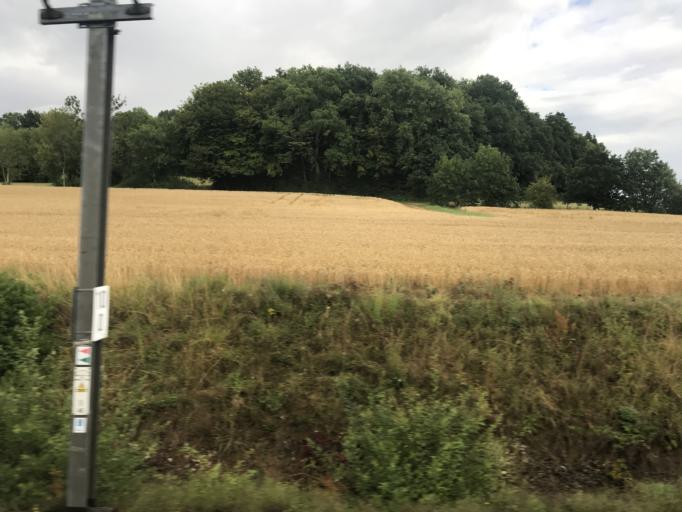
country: LU
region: Luxembourg
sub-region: Canton d'Esch-sur-Alzette
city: Reckange-sur-Mess
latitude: 49.5756
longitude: 6.0035
